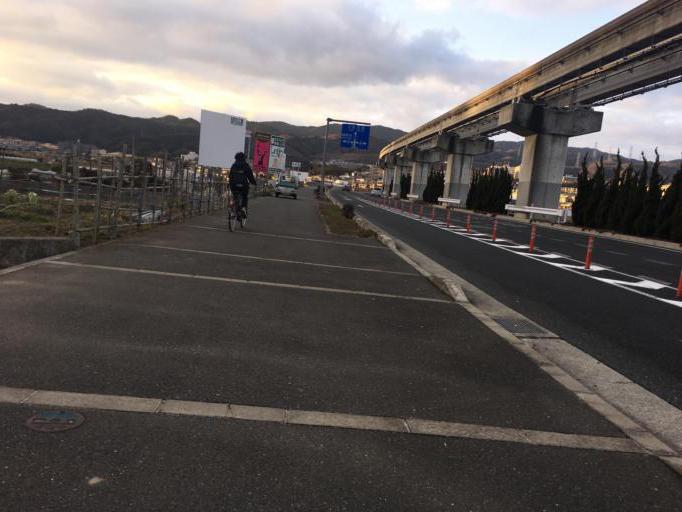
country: JP
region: Osaka
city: Ibaraki
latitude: 34.8421
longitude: 135.5232
